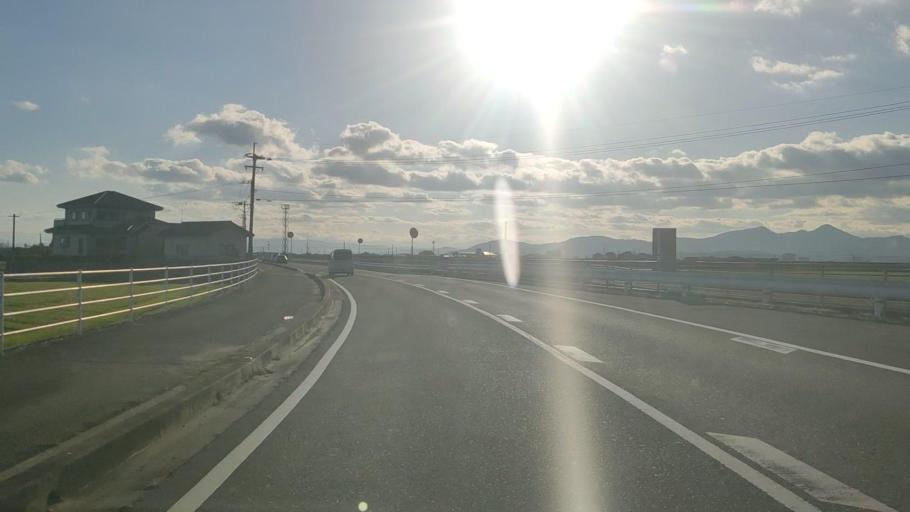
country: JP
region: Saga Prefecture
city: Saga-shi
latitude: 33.2909
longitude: 130.2358
